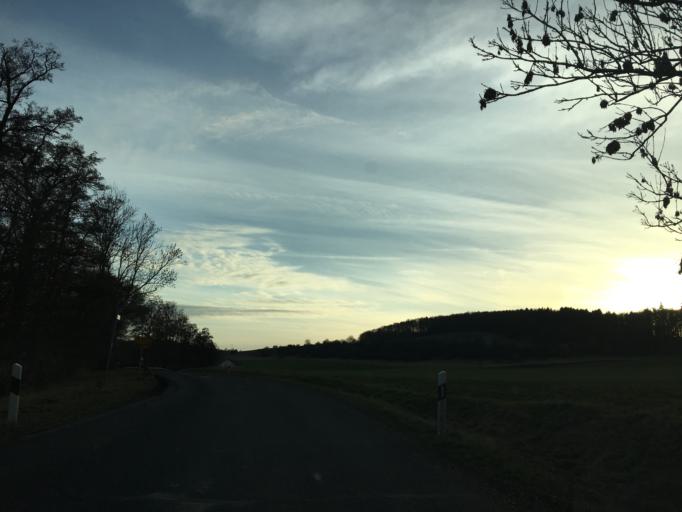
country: DE
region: Hesse
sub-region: Regierungsbezirk Giessen
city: Alsfeld
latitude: 50.6915
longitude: 9.3023
